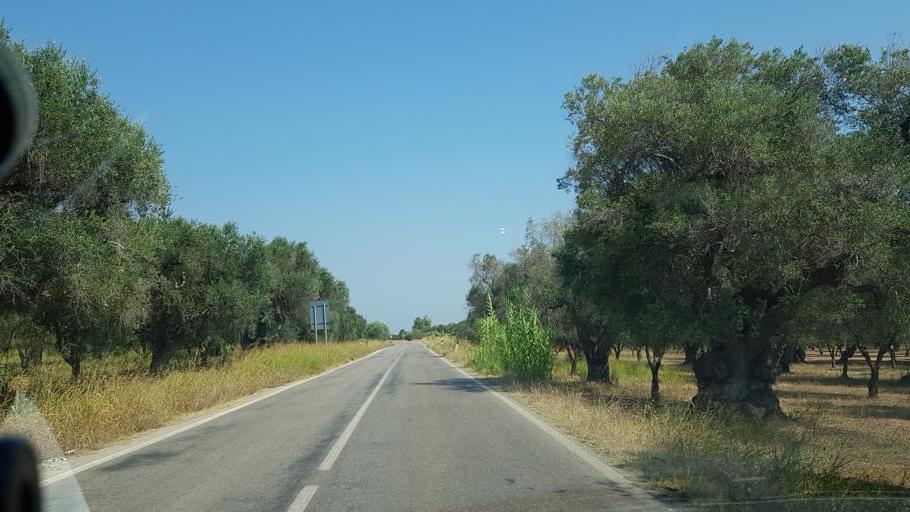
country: IT
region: Apulia
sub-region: Provincia di Brindisi
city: Torre Santa Susanna
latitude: 40.4976
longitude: 17.7452
